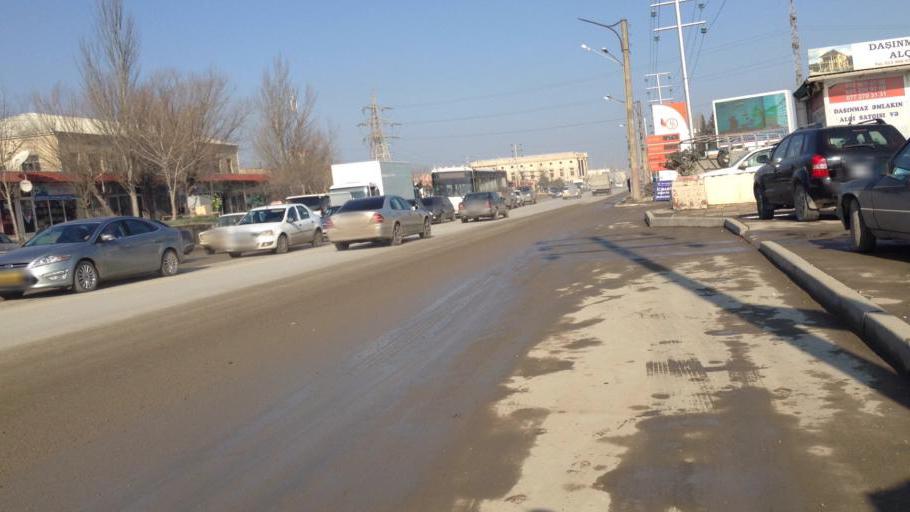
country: AZ
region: Baki
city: Binagadi
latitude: 40.4412
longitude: 49.8450
